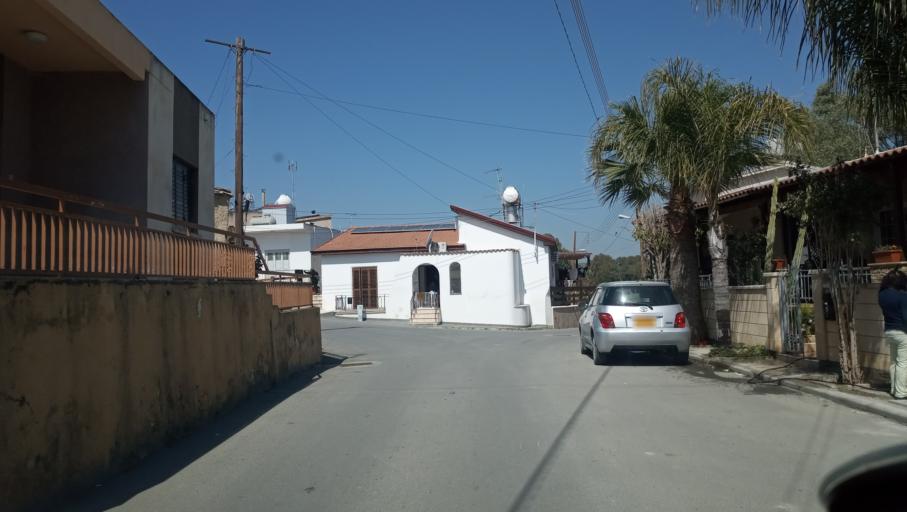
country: CY
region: Lefkosia
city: Alampra
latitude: 35.0142
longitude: 33.3892
